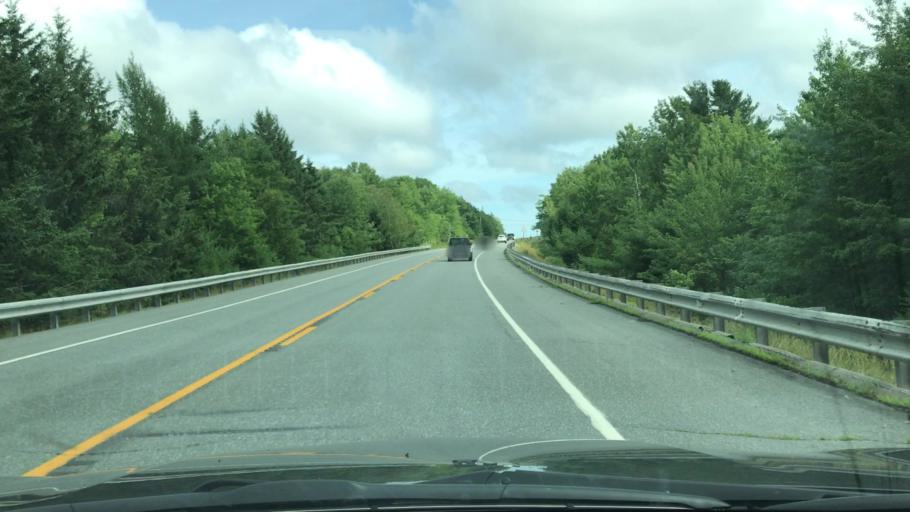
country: US
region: Maine
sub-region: Hancock County
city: Surry
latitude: 44.5560
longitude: -68.5423
